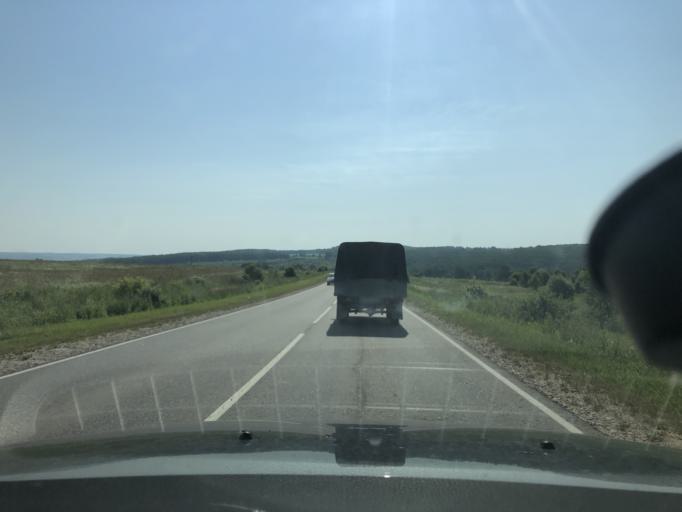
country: RU
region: Tula
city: Dubna
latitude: 54.1320
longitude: 37.0331
